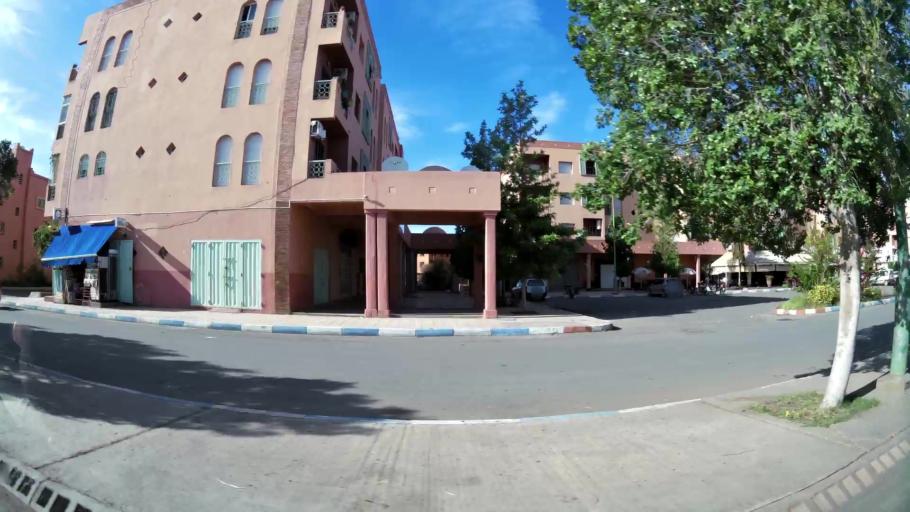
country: MA
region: Marrakech-Tensift-Al Haouz
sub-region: Marrakech
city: Marrakesh
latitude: 31.6831
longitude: -8.0674
